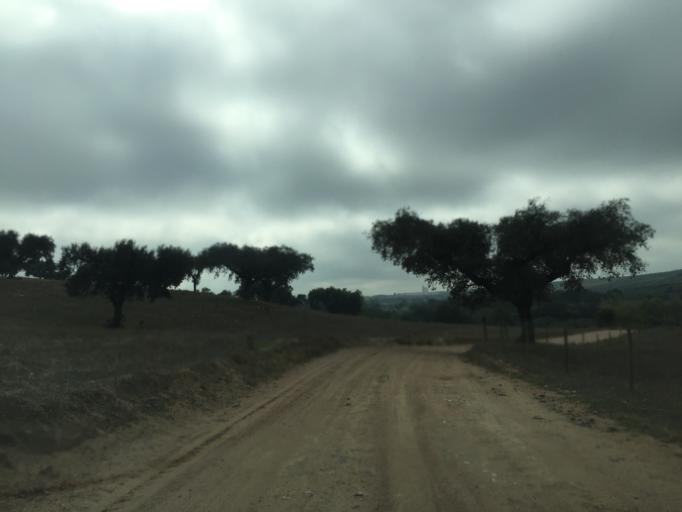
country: PT
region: Portalegre
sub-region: Fronteira
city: Fronteira
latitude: 39.0680
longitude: -7.6239
